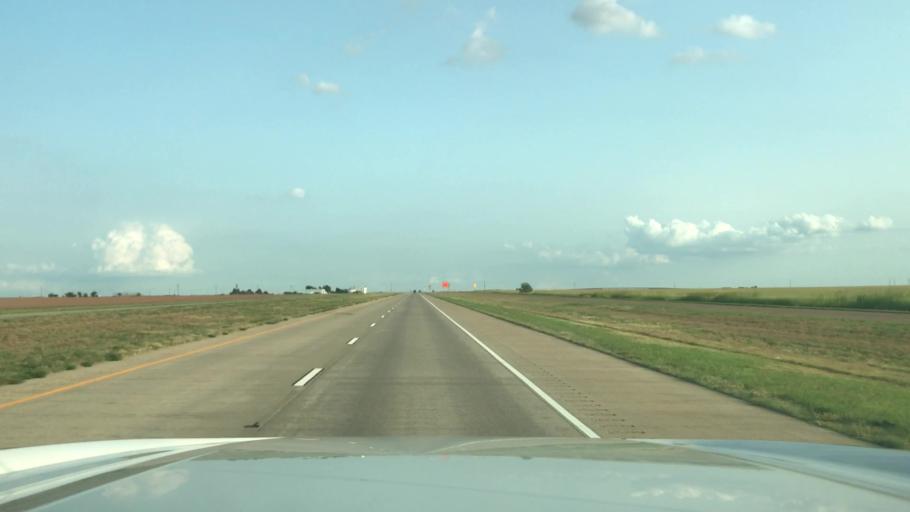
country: US
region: Texas
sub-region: Swisher County
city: Tulia
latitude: 34.4935
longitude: -101.7822
